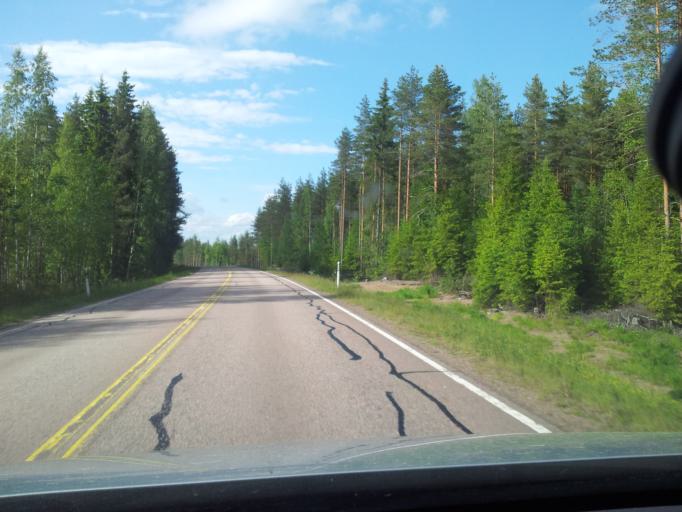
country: FI
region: South Karelia
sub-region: Lappeenranta
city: Luumaeki
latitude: 60.9439
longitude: 27.5855
